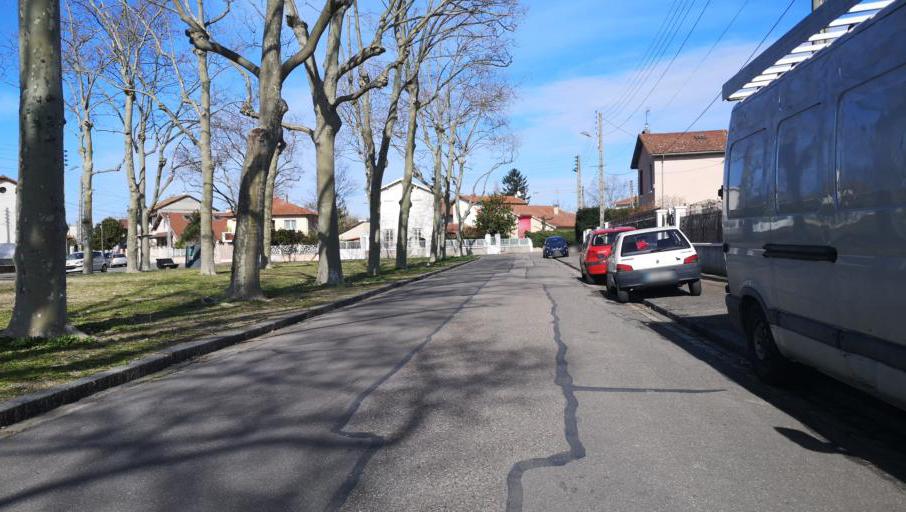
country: FR
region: Rhone-Alpes
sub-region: Departement du Rhone
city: Villeurbanne
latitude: 45.7749
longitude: 4.8960
